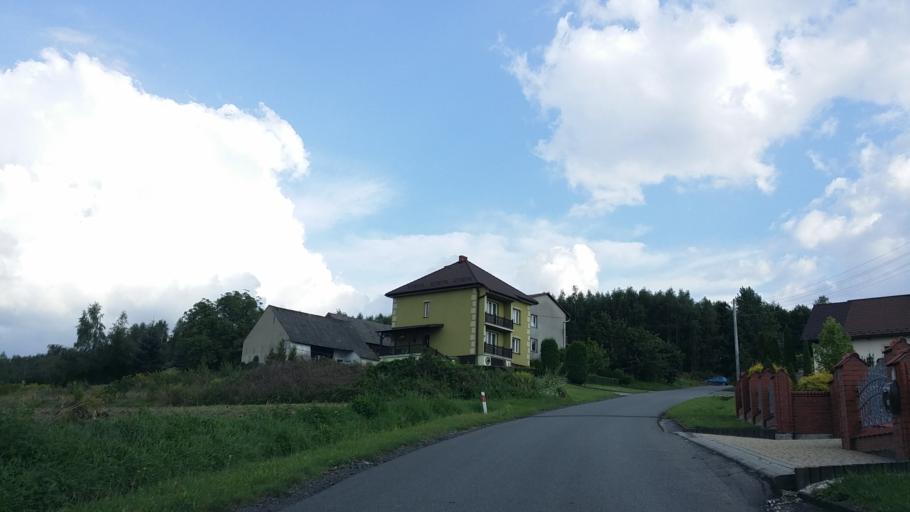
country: PL
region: Lesser Poland Voivodeship
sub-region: Powiat wadowicki
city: Spytkowice
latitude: 49.9907
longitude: 19.4761
